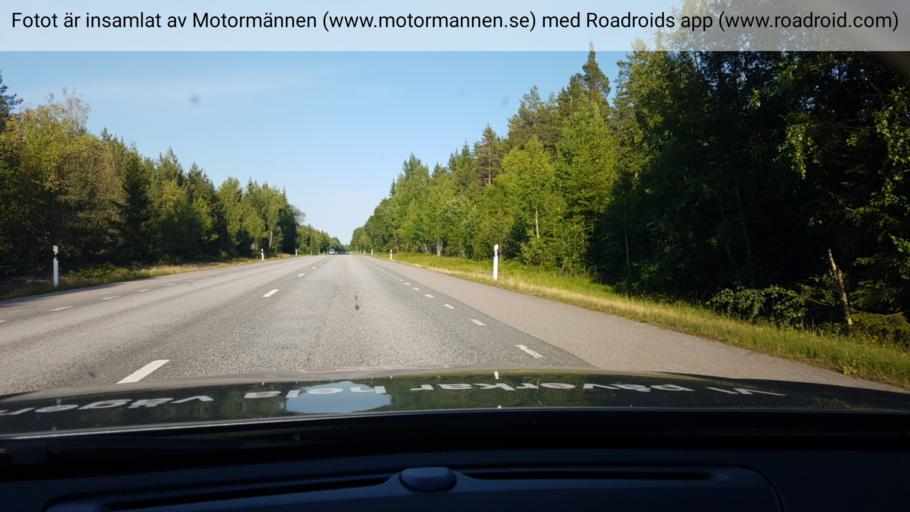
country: SE
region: Uppsala
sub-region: Osthammars Kommun
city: Gimo
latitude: 60.1644
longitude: 18.1123
